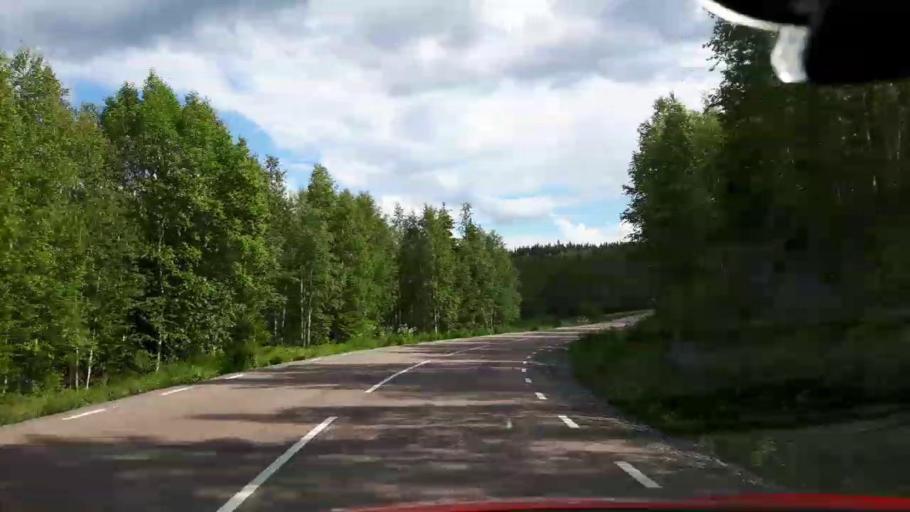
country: SE
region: Jaemtland
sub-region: Krokoms Kommun
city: Valla
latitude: 63.9466
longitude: 14.2255
